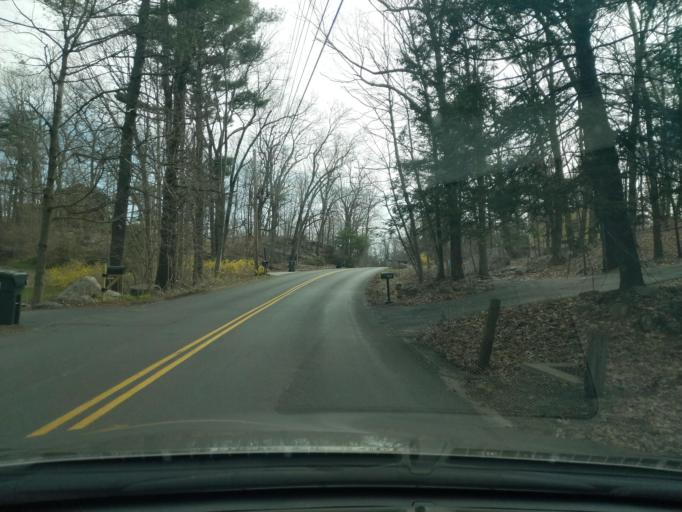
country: US
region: Connecticut
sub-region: Fairfield County
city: Newtown
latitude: 41.3409
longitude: -73.2424
